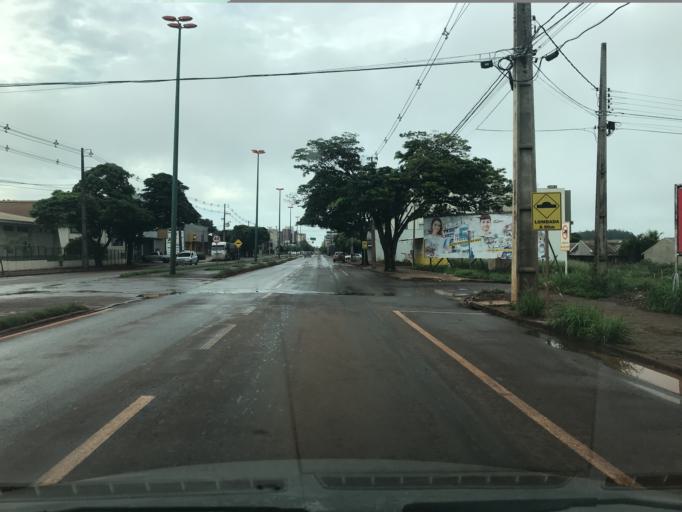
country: BR
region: Parana
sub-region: Palotina
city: Palotina
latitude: -24.2918
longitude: -53.8372
